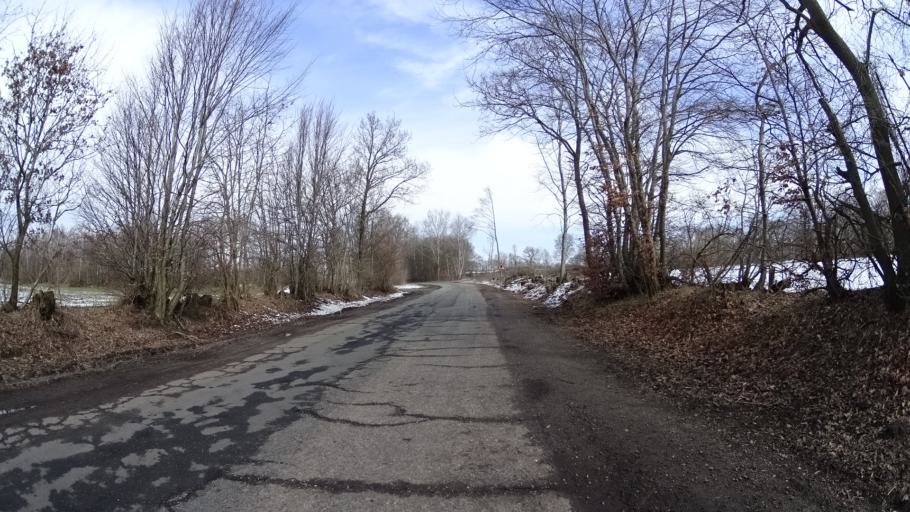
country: DE
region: Schleswig-Holstein
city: Gross Kummerfeld
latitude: 54.0317
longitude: 10.1148
